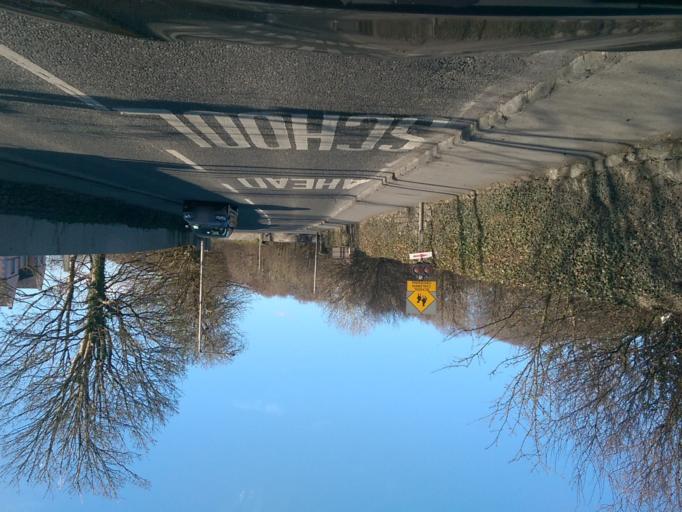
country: IE
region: Connaught
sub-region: County Galway
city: Oranmore
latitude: 53.2273
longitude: -8.8795
